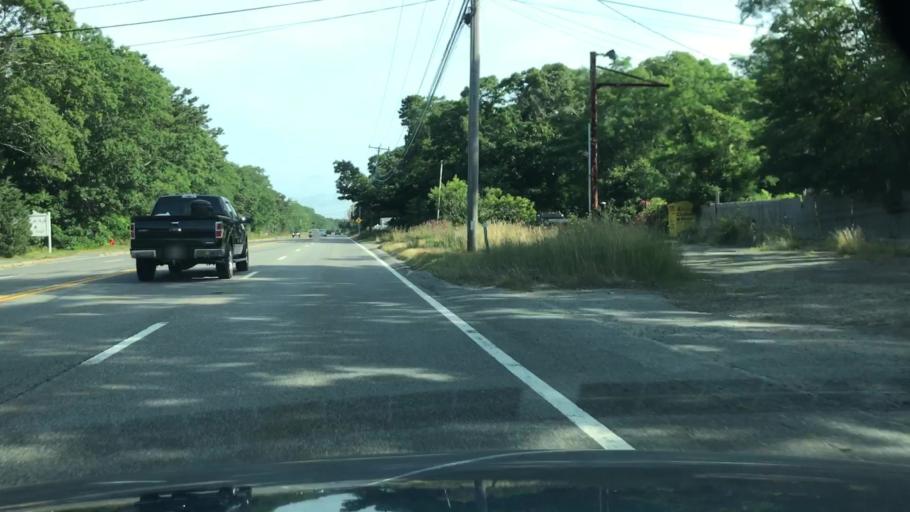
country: US
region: Massachusetts
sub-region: Barnstable County
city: North Eastham
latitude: 41.8686
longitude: -69.9850
